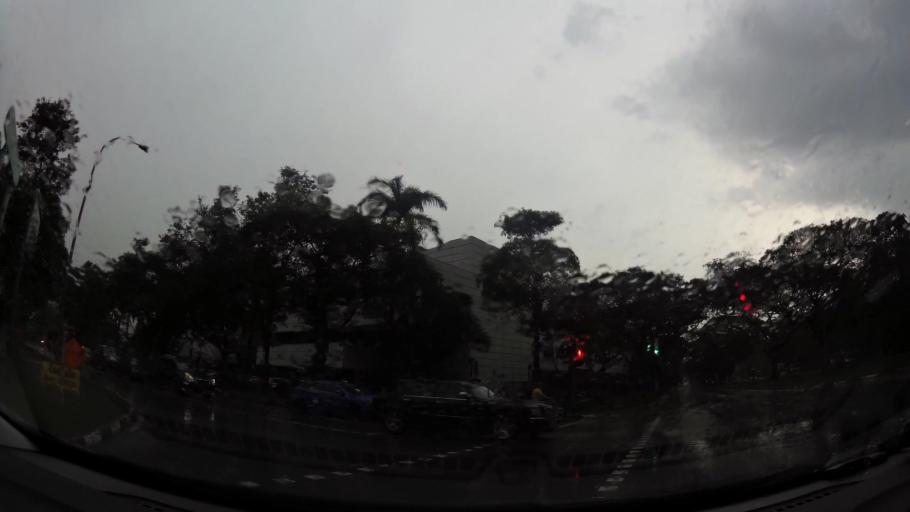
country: MY
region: Johor
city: Kampung Pasir Gudang Baru
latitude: 1.3902
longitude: 103.8452
